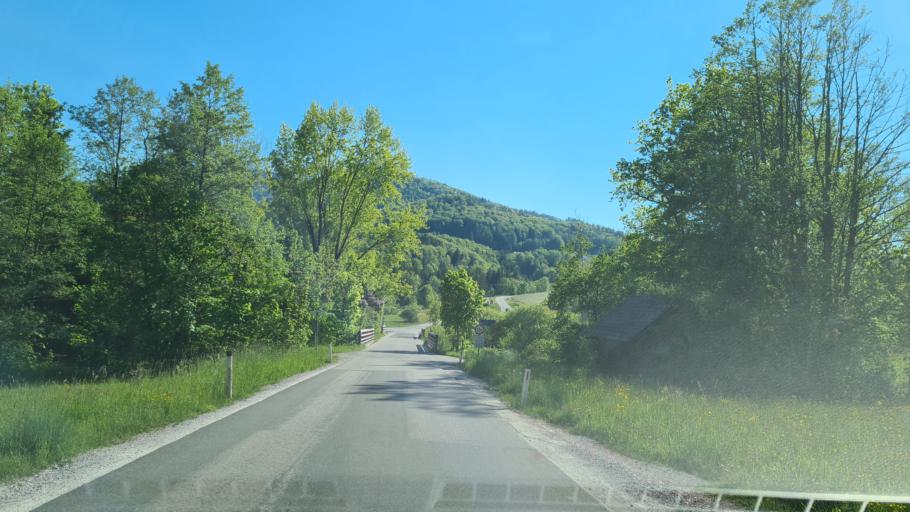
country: AT
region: Salzburg
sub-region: Politischer Bezirk Salzburg-Umgebung
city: Thalgau
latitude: 47.8205
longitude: 13.2451
